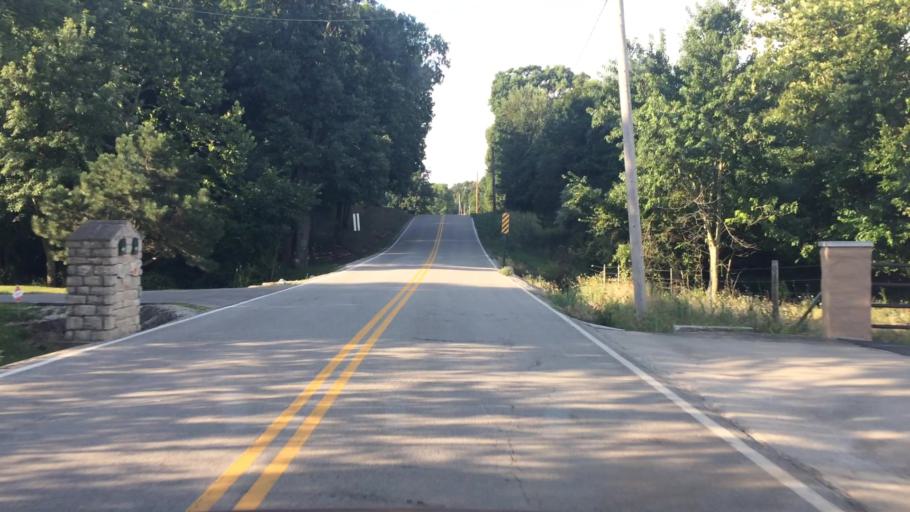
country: US
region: Missouri
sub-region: Greene County
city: Strafford
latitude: 37.2598
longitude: -93.1878
